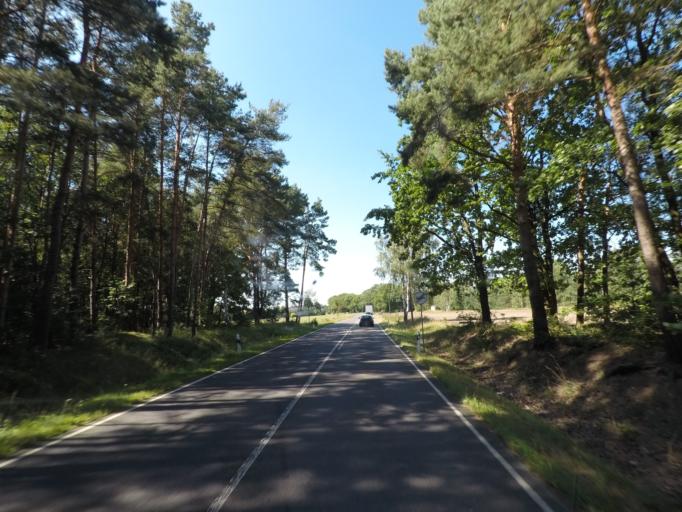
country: DE
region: Brandenburg
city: Welzow
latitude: 51.5552
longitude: 14.1403
